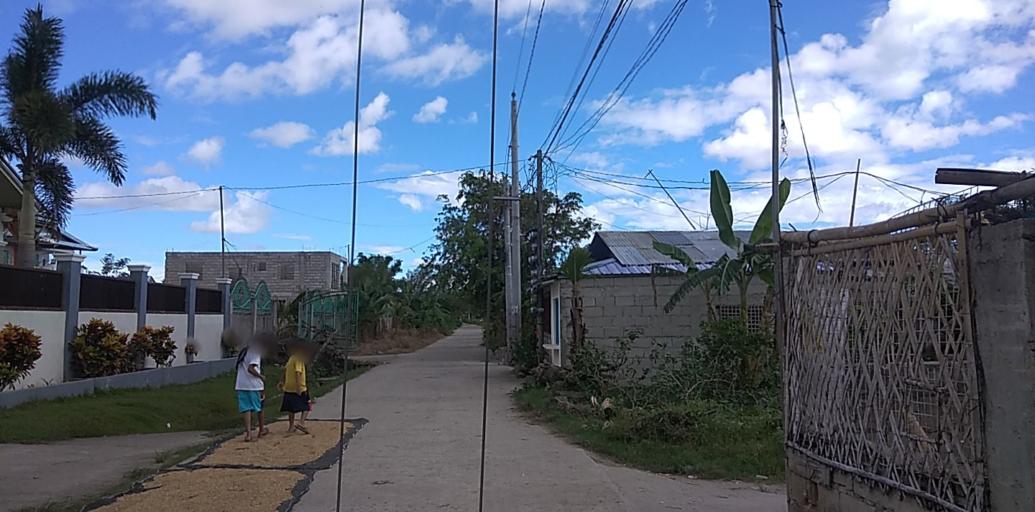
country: PH
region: Central Luzon
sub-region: Province of Pampanga
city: Arayat
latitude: 15.1348
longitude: 120.7807
